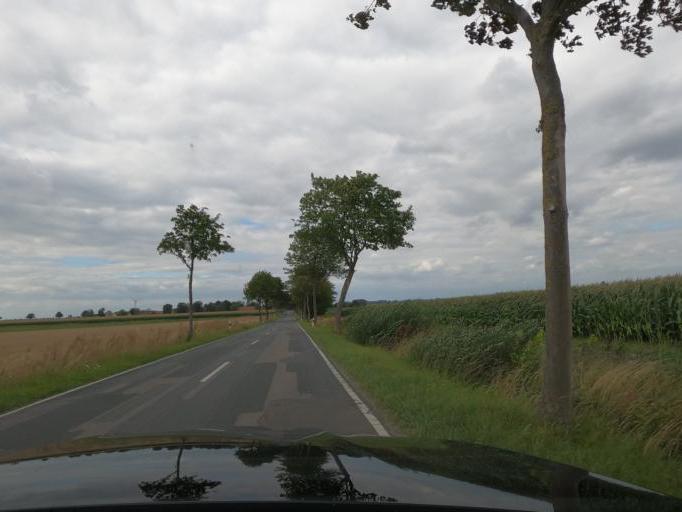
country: DE
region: Lower Saxony
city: Ilsede
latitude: 52.2122
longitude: 10.1709
